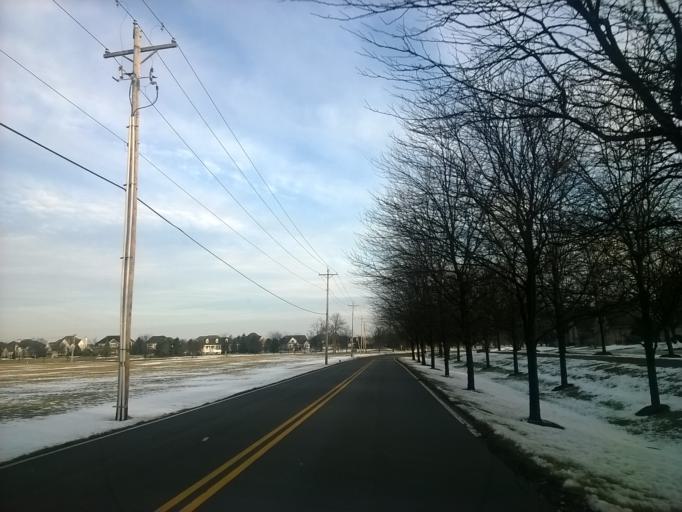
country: US
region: Indiana
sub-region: Hamilton County
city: Fishers
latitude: 39.9763
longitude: -86.0516
